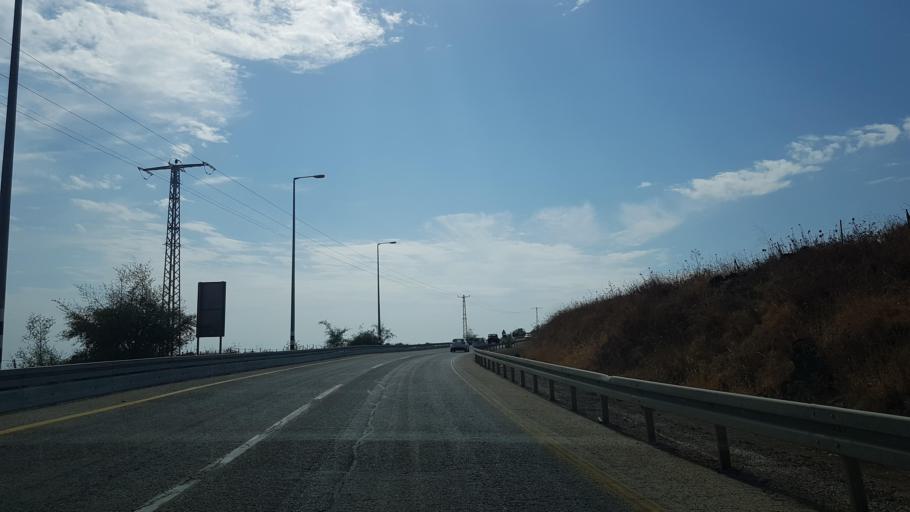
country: SY
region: Quneitra
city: Al Butayhah
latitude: 32.9134
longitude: 35.5871
